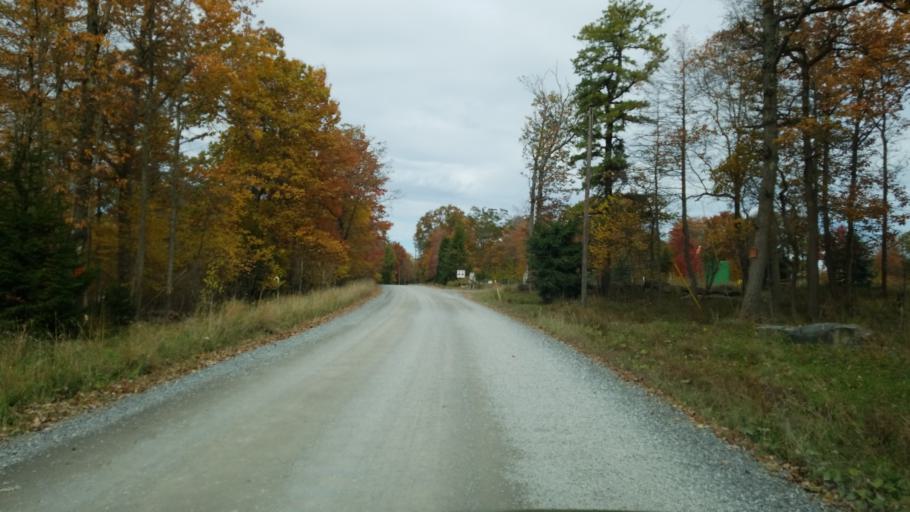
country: US
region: Pennsylvania
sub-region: Clearfield County
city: Clearfield
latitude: 41.1720
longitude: -78.4442
